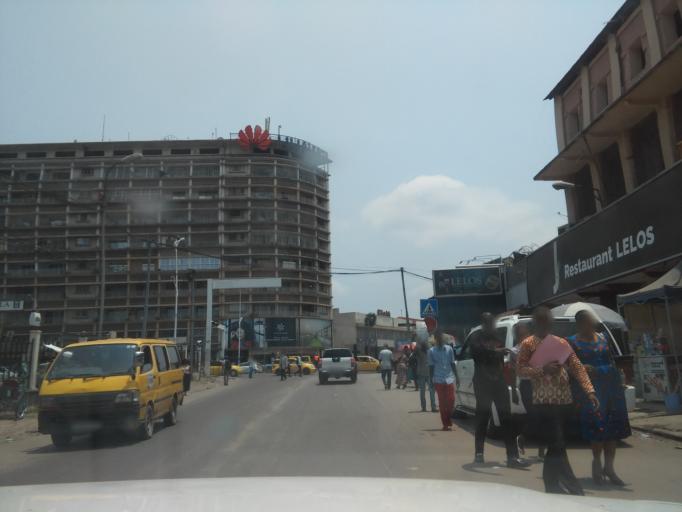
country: CD
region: Kinshasa
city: Kinshasa
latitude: -4.3046
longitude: 15.3084
